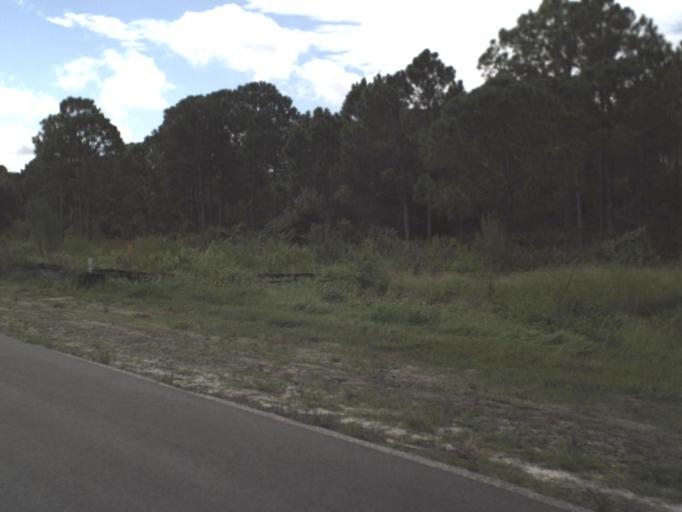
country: US
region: Florida
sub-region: Sarasota County
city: Warm Mineral Springs
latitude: 27.1090
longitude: -82.3100
